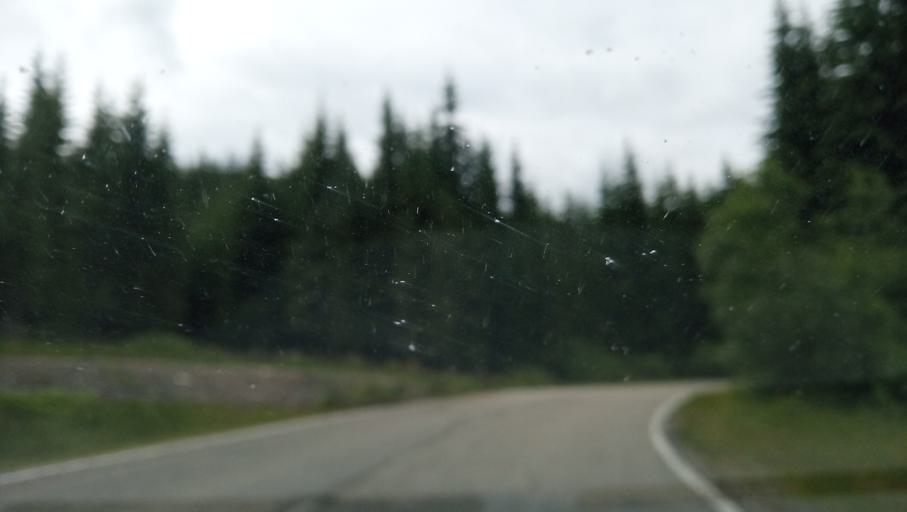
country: RO
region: Valcea
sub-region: Comuna Voineasa
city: Voineasa
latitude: 45.4238
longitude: 23.7674
